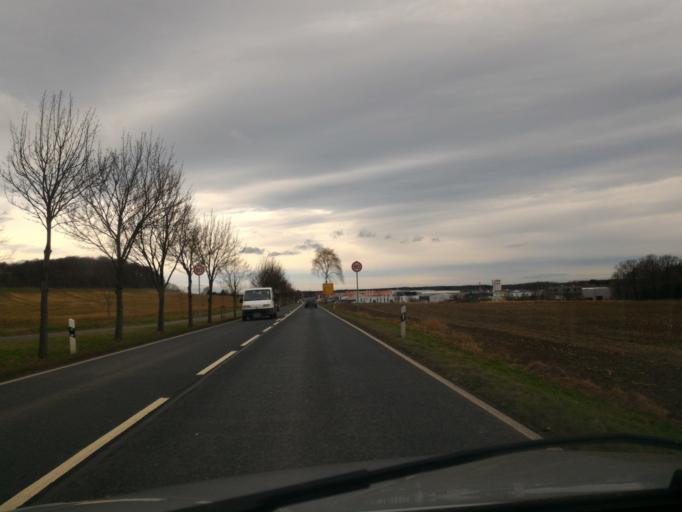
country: DE
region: Saxony
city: Radeberg
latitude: 51.0634
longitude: 13.9044
